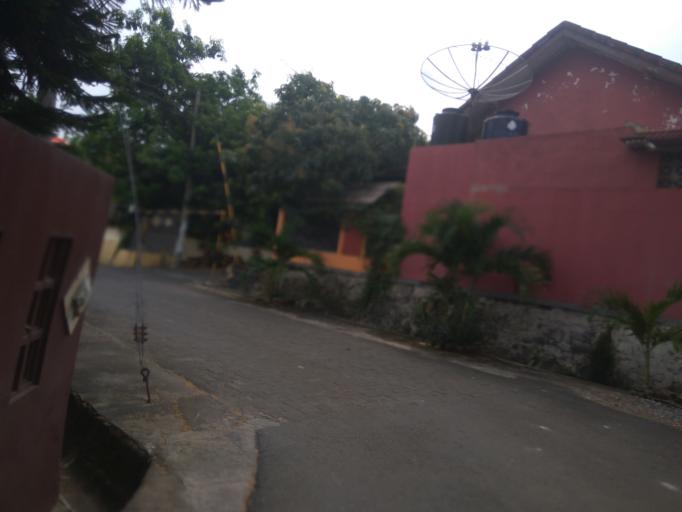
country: ID
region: Central Java
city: Semarang
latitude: -7.0641
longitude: 110.4472
